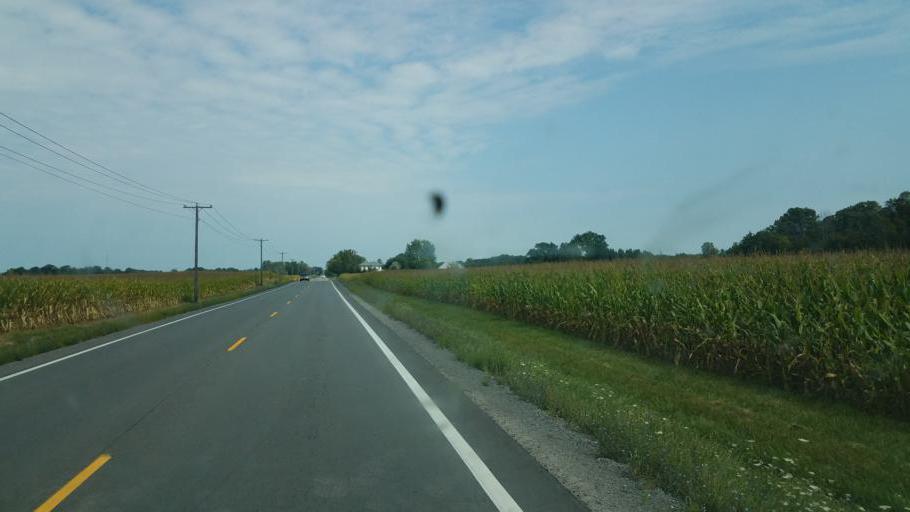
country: US
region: Ohio
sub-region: Marion County
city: Marion
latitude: 40.4961
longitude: -83.0654
